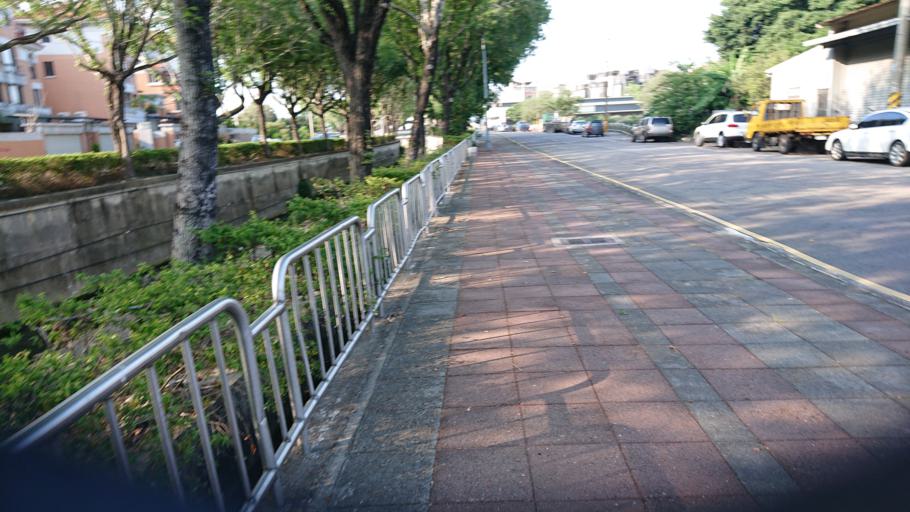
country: TW
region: Taiwan
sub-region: Taichung City
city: Taichung
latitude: 24.1136
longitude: 120.6302
